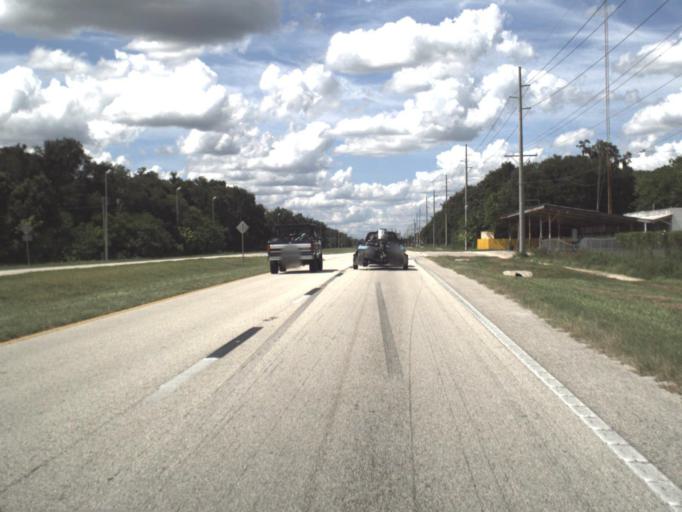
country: US
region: Florida
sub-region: Polk County
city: Willow Oak
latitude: 27.9098
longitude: -82.0152
